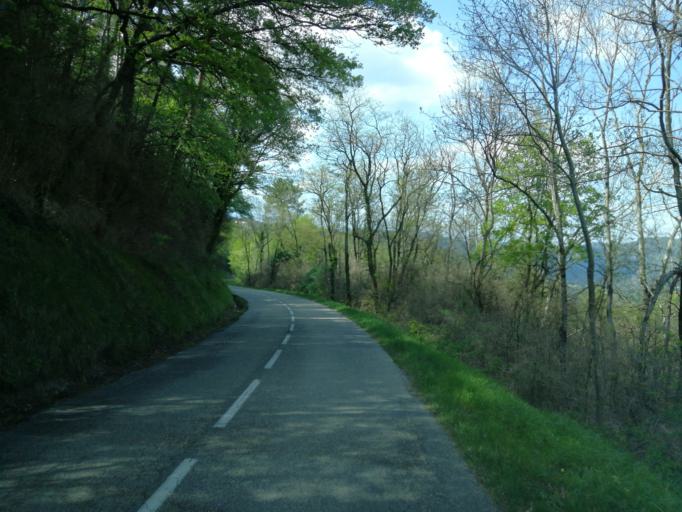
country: FR
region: Rhone-Alpes
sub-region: Departement de l'Ardeche
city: Saint-Sauveur-de-Montagut
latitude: 44.7872
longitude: 4.6154
